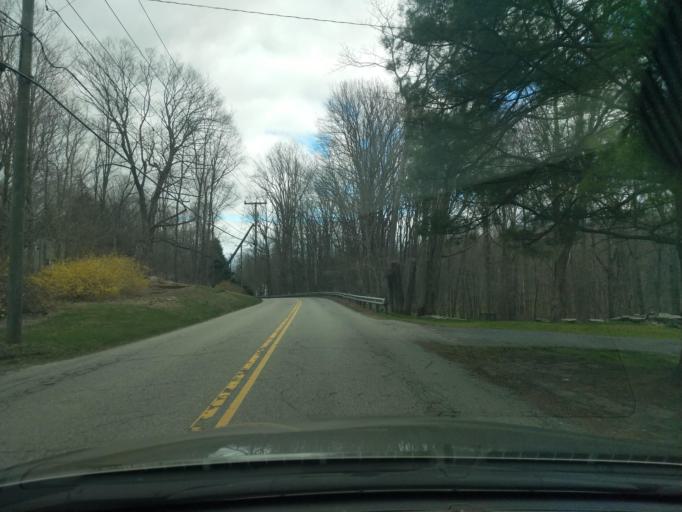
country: US
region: Connecticut
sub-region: Fairfield County
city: Newtown
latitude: 41.3459
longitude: -73.3162
